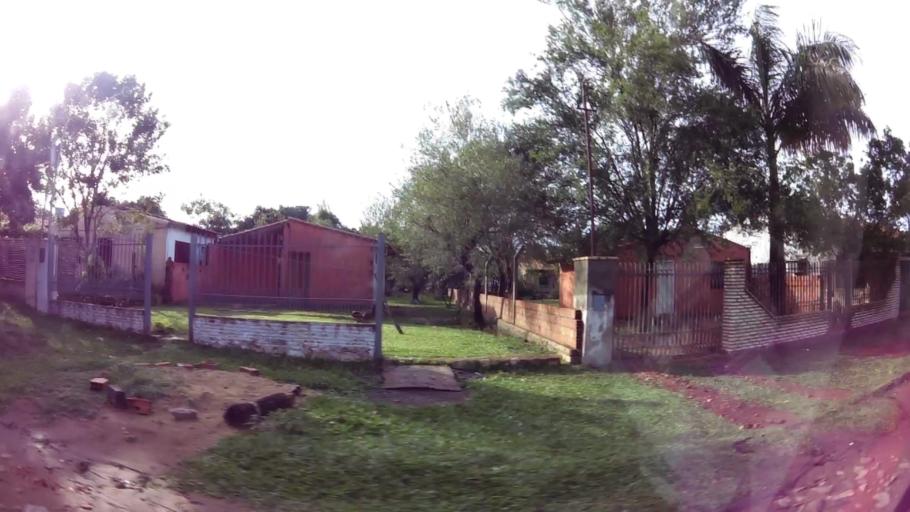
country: PY
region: Central
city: Limpio
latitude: -25.1872
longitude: -57.4823
